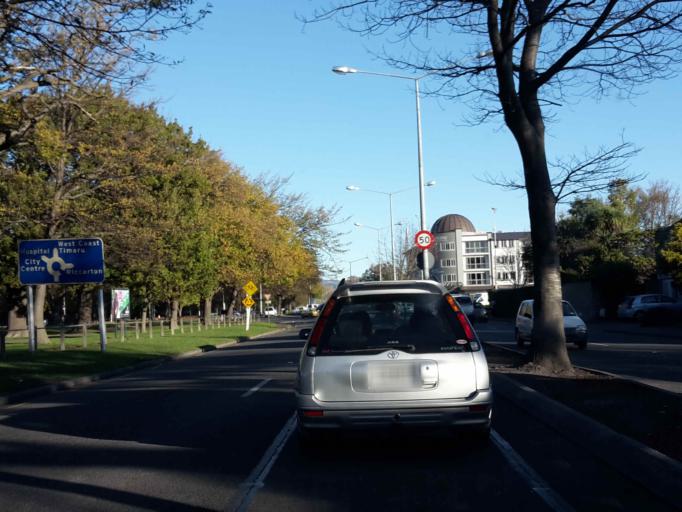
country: NZ
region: Canterbury
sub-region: Christchurch City
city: Christchurch
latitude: -43.5276
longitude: 172.6124
